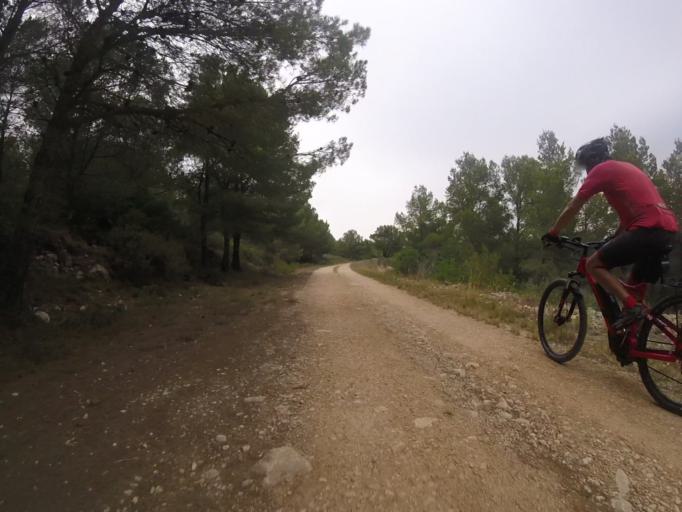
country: ES
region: Valencia
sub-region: Provincia de Castello
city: Alcoceber
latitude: 40.2813
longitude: 0.2832
